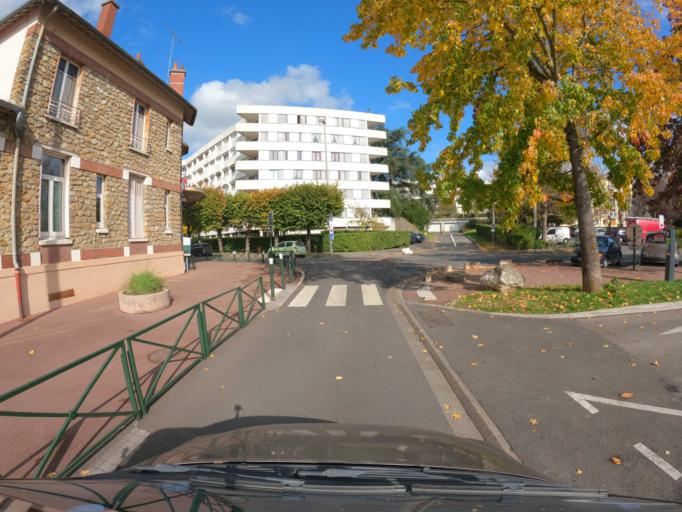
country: FR
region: Ile-de-France
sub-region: Departement de Seine-et-Marne
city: Chelles
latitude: 48.8785
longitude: 2.5953
